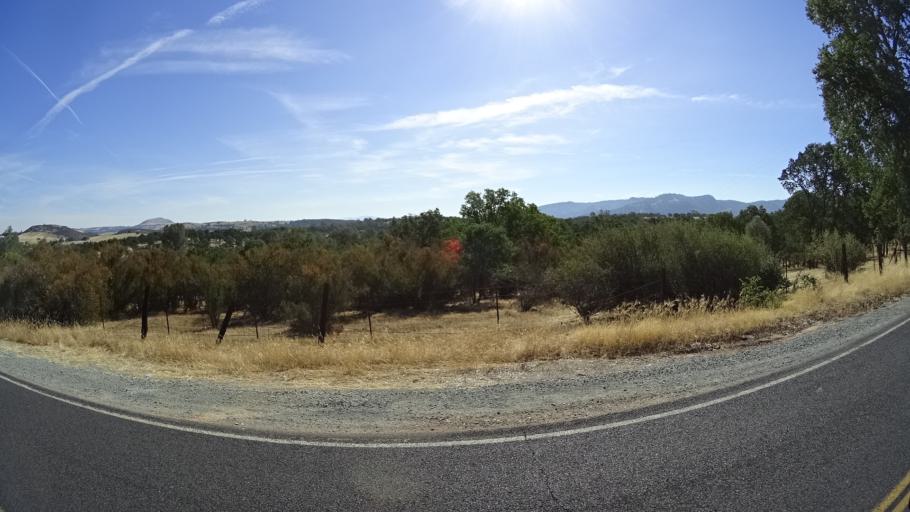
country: US
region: California
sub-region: Calaveras County
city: Valley Springs
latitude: 38.1782
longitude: -120.8126
